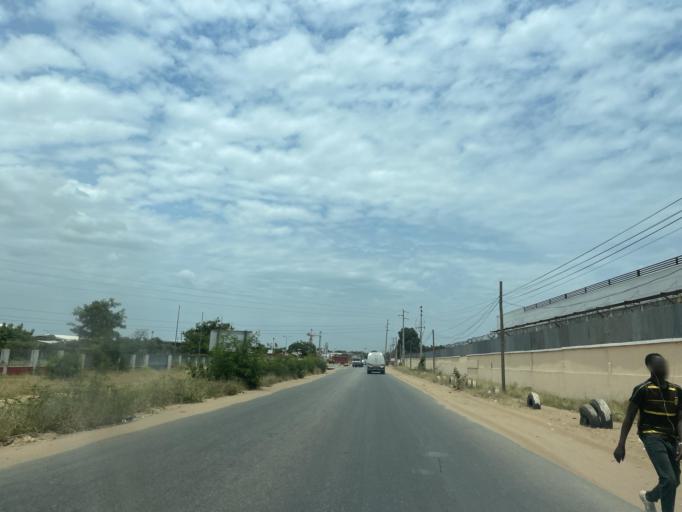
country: AO
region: Luanda
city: Luanda
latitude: -8.9345
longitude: 13.3915
